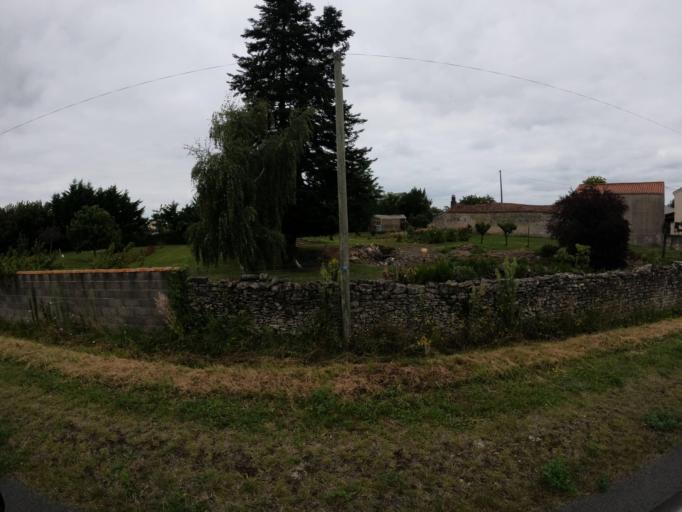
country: FR
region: Pays de la Loire
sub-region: Departement de la Vendee
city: Serigne
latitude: 46.4706
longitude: -0.8549
